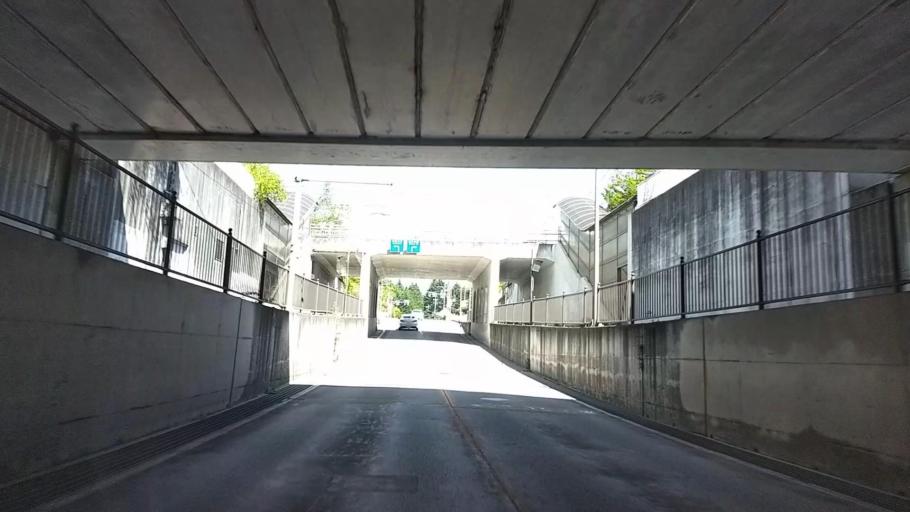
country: JP
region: Nagano
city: Saku
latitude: 36.3430
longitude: 138.6304
